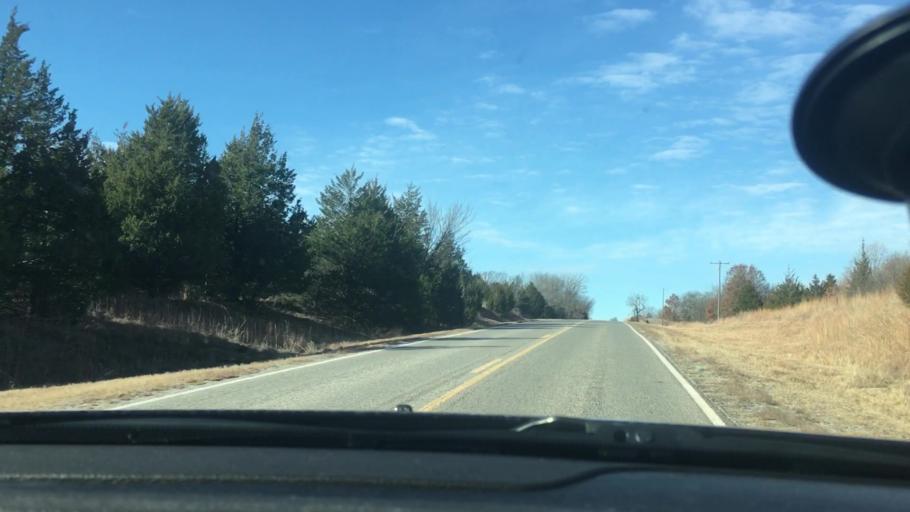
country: US
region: Oklahoma
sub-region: Seminole County
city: Konawa
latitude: 34.9858
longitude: -96.8942
